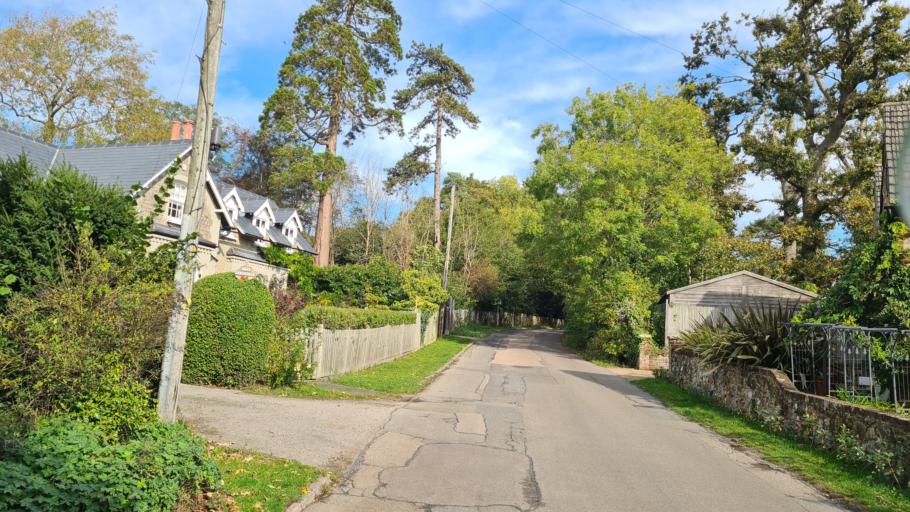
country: GB
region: England
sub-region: East Sussex
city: Hastings
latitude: 50.8792
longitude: 0.5615
